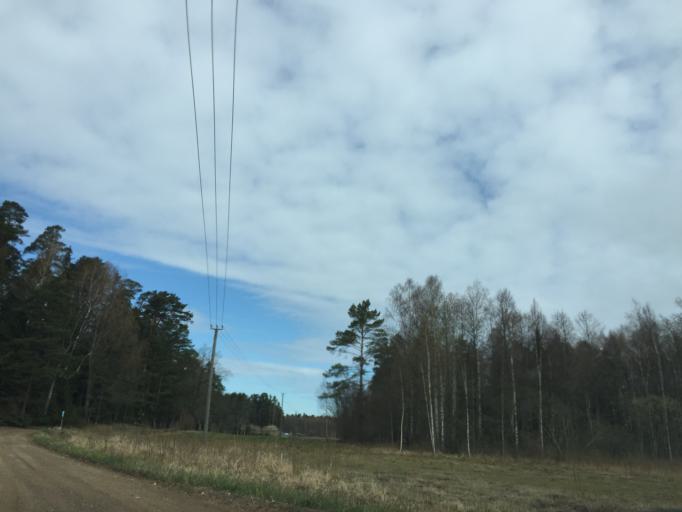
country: LV
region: Salacgrivas
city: Salacgriva
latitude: 57.5292
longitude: 24.3773
